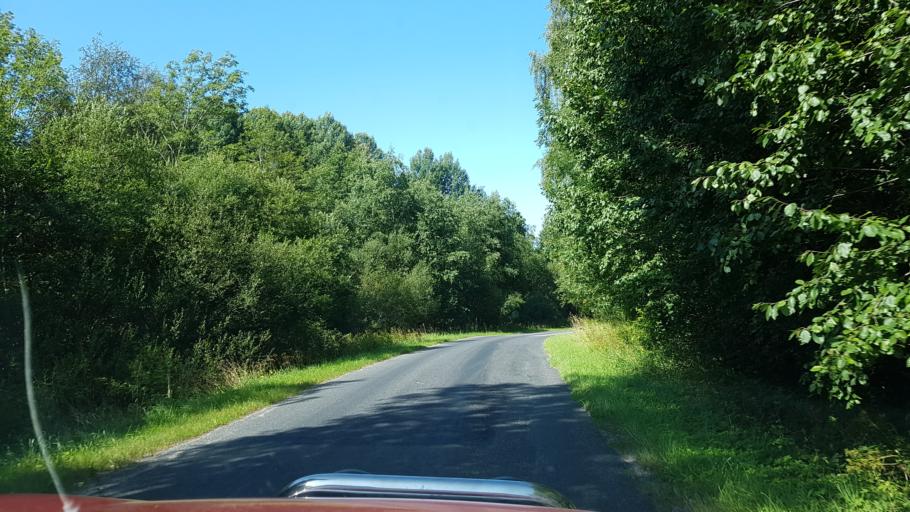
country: EE
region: Vorumaa
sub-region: Voru linn
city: Voru
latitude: 57.7893
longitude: 27.2410
